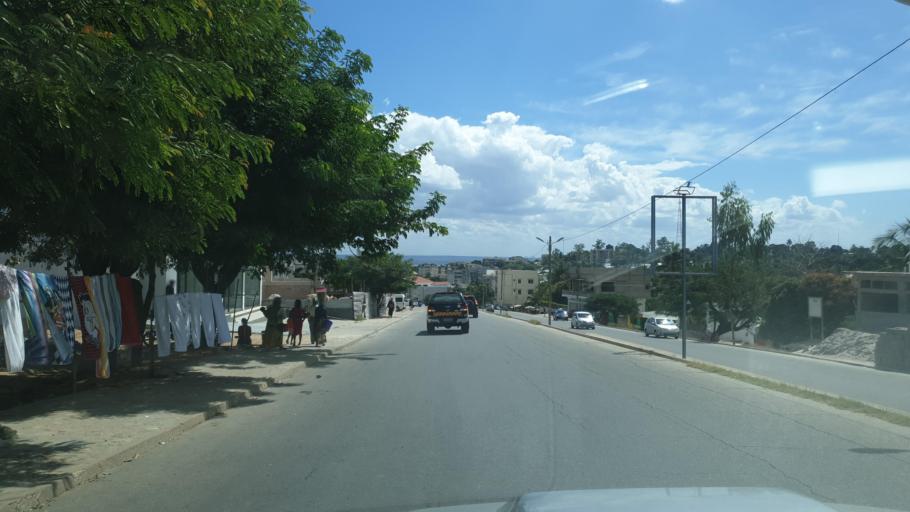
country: MZ
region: Nampula
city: Nacala
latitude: -14.5454
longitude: 40.6835
